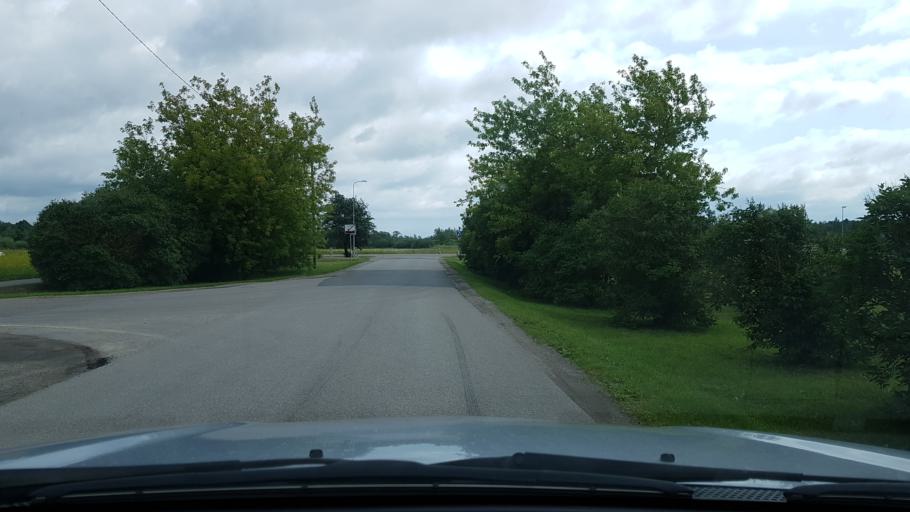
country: EE
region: Ida-Virumaa
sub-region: Narva linn
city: Narva
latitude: 59.3900
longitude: 28.1309
